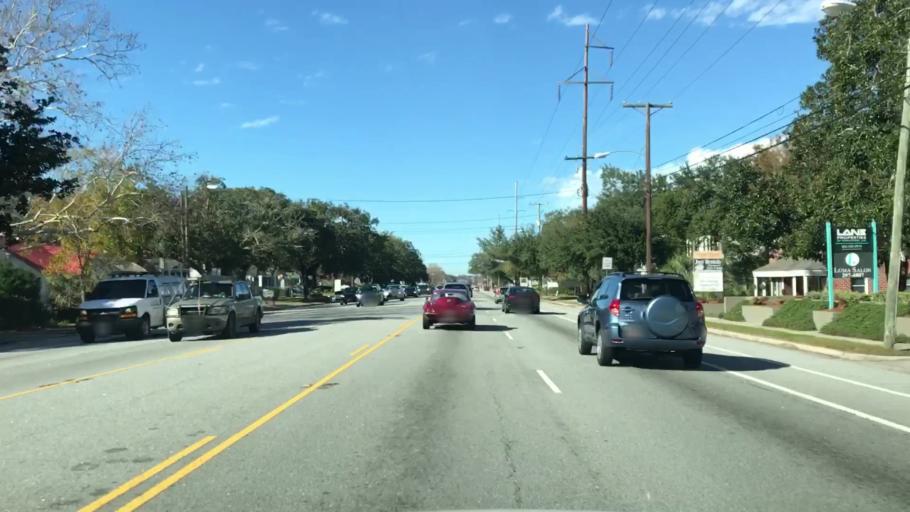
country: US
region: South Carolina
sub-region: Charleston County
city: Charleston
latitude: 32.7884
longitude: -79.9834
